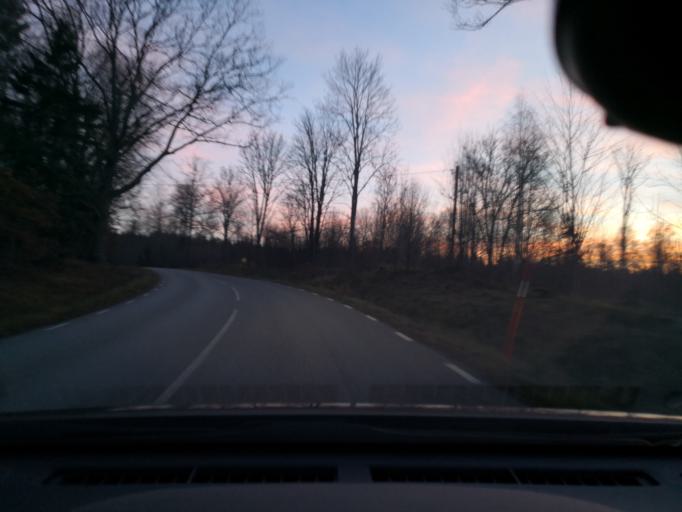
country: SE
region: OErebro
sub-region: Lindesbergs Kommun
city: Fellingsbro
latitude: 59.4220
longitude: 15.5640
